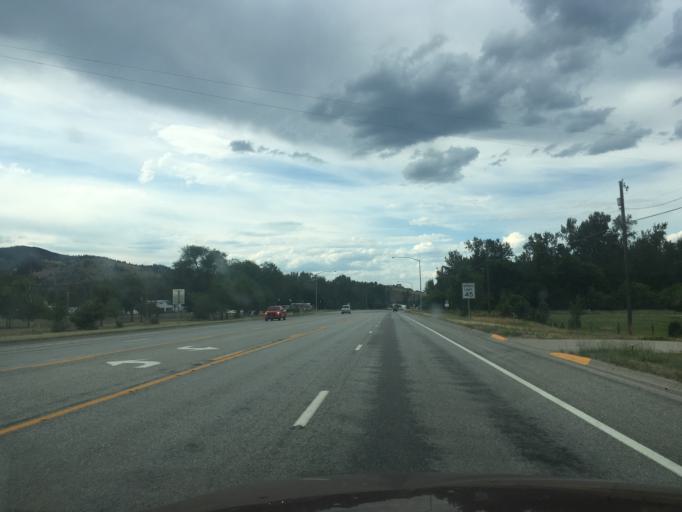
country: US
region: Montana
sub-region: Missoula County
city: Lolo
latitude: 46.7459
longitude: -114.0822
